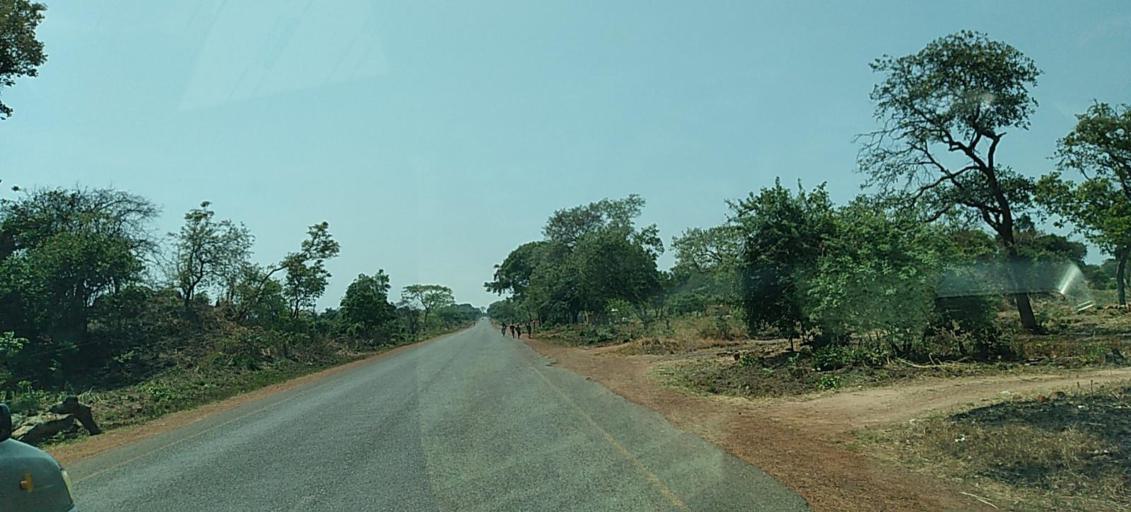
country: ZM
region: North-Western
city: Solwezi
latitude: -12.3180
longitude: 25.8644
